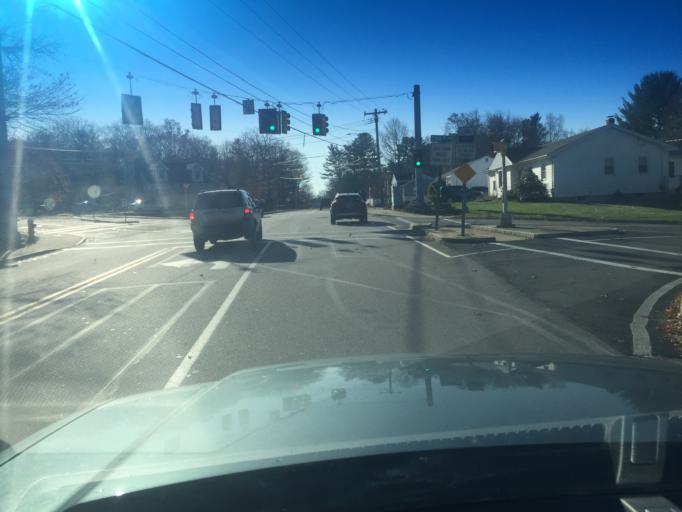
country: US
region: Massachusetts
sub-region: Norfolk County
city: Franklin
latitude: 42.1052
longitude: -71.4286
